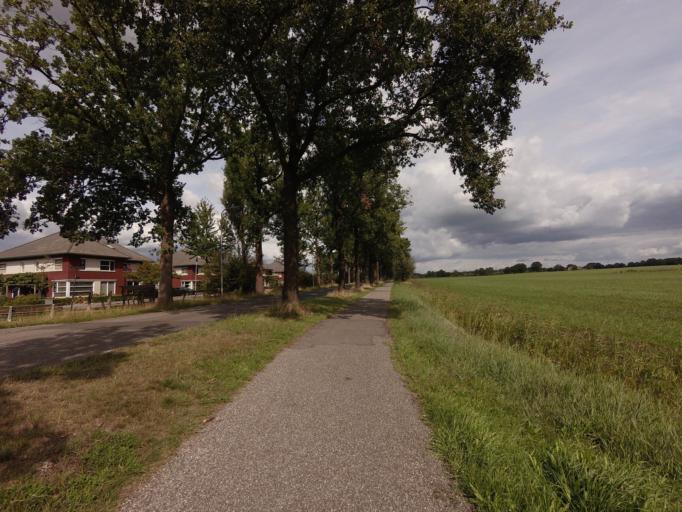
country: NL
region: Overijssel
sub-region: Gemeente Deventer
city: Schalkhaar
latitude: 52.2756
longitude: 6.2050
